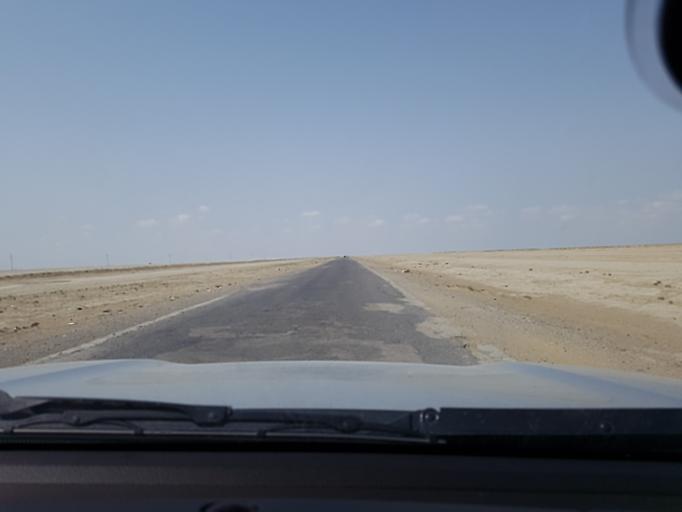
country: TM
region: Balkan
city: Gumdag
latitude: 38.6726
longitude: 54.4075
